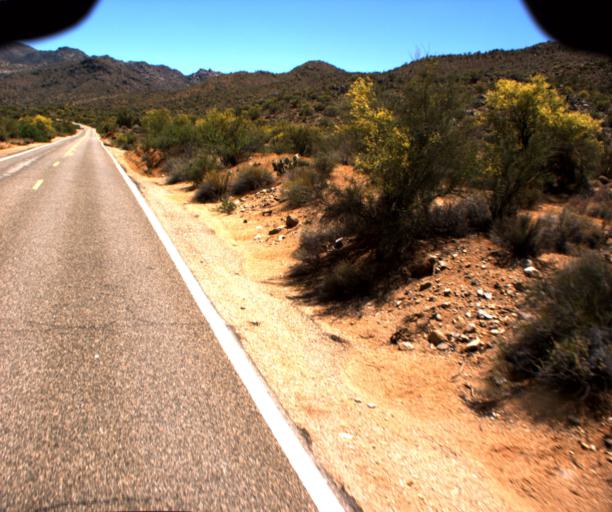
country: US
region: Arizona
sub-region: Yavapai County
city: Bagdad
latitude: 34.4637
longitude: -113.0432
